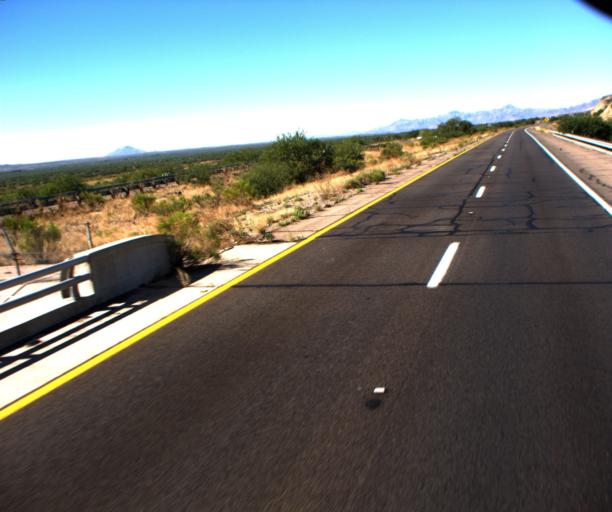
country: US
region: Arizona
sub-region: Pima County
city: Green Valley
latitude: 31.7899
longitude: -111.0218
